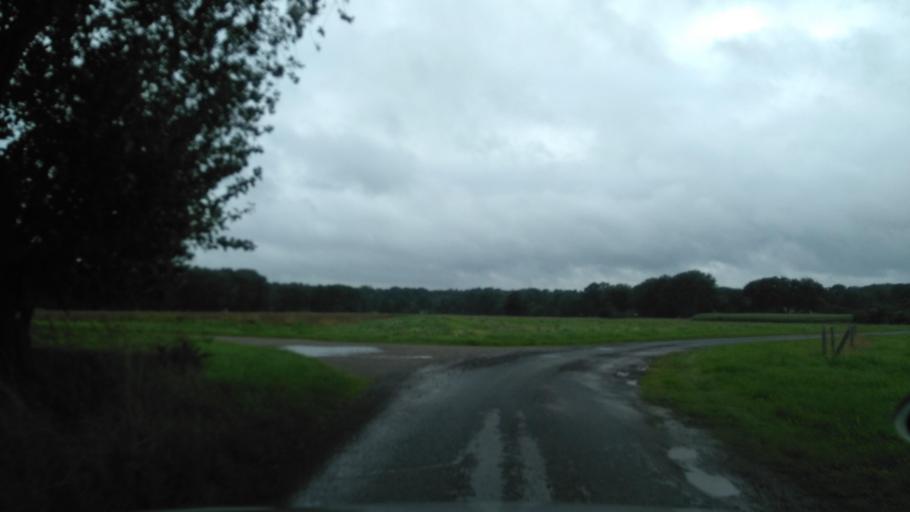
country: DE
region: Lower Saxony
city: Walsrode
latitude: 52.8923
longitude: 9.6013
